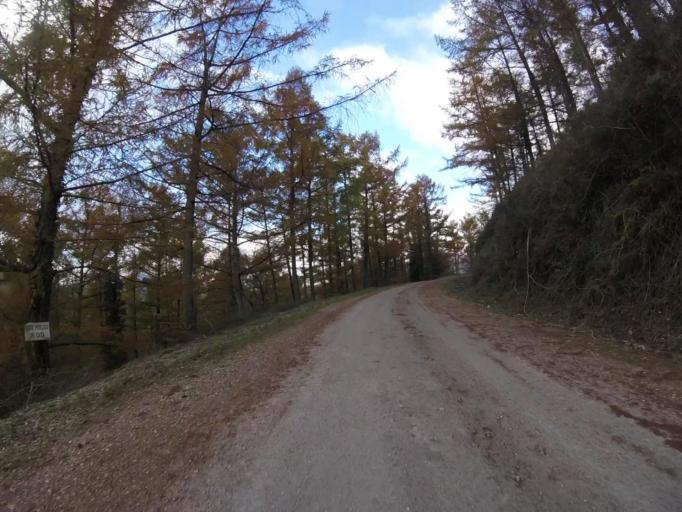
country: ES
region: Navarre
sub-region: Provincia de Navarra
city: Arano
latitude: 43.2134
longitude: -1.8577
